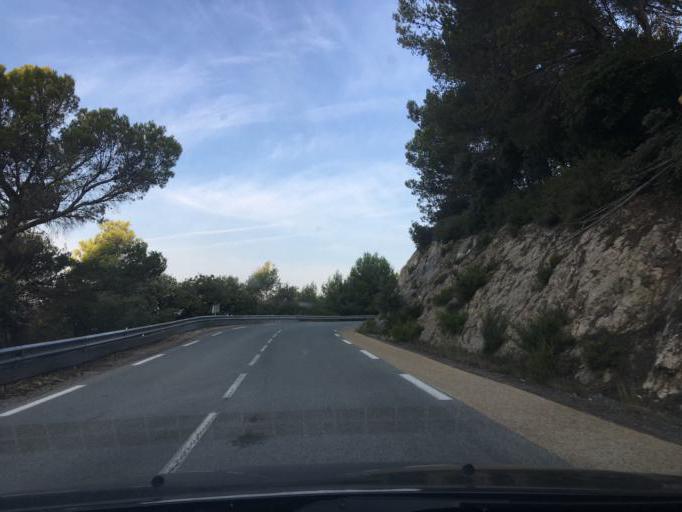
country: FR
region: Provence-Alpes-Cote d'Azur
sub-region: Departement du Var
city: Aups
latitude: 43.6577
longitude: 6.2224
